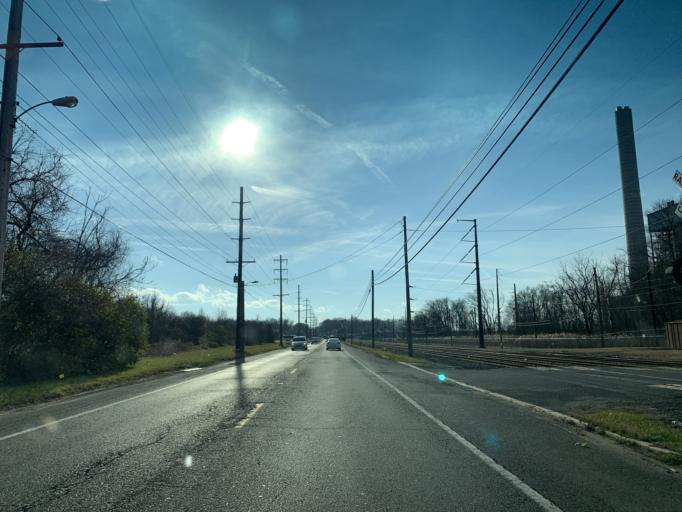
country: US
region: New Jersey
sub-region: Salem County
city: Carneys Point
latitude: 39.6943
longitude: -75.4823
